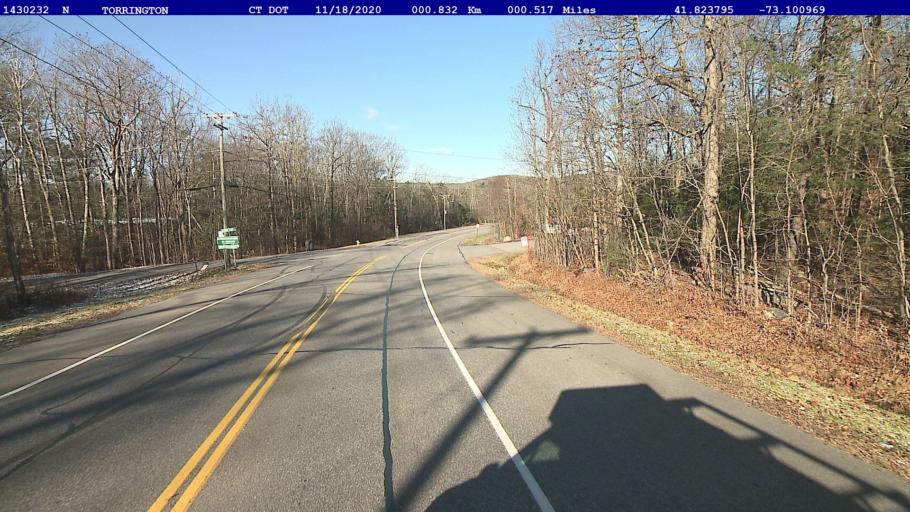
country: US
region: Connecticut
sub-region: Litchfield County
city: Torrington
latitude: 41.8238
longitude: -73.1010
